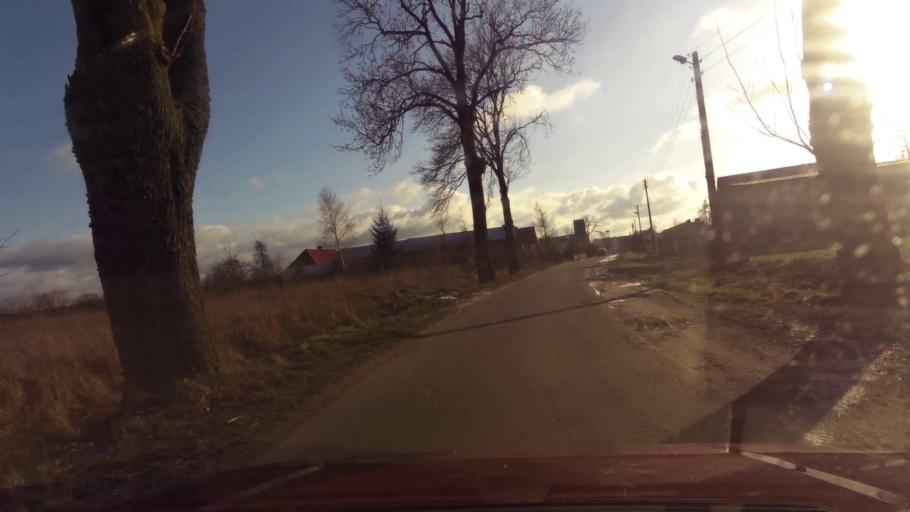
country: PL
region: West Pomeranian Voivodeship
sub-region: Powiat bialogardzki
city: Bialogard
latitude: 54.0749
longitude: 16.0903
